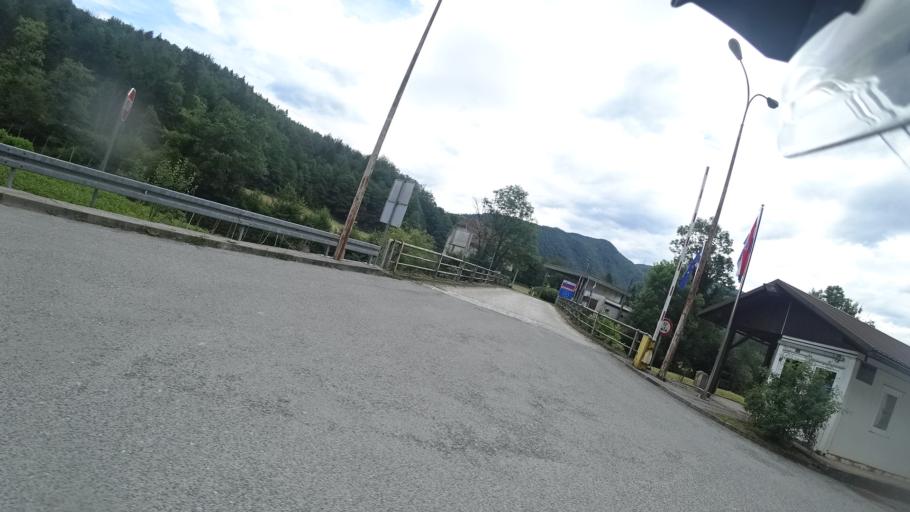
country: SI
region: Osilnica
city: Osilnica
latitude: 45.5325
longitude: 14.6858
